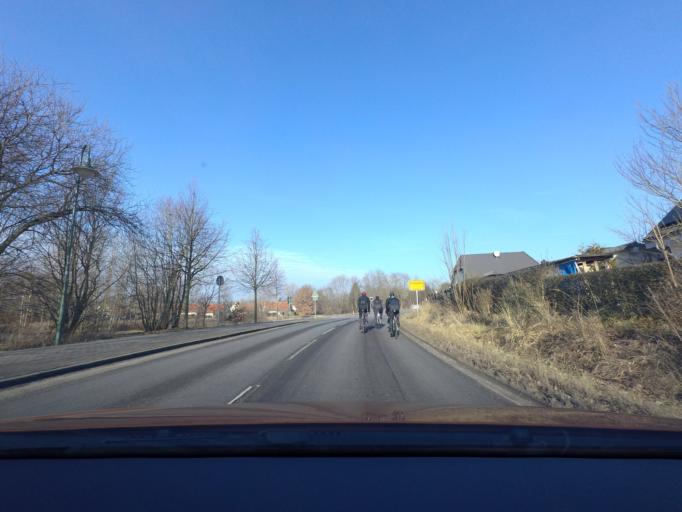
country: DE
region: Berlin
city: Blankenfelde
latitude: 52.6581
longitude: 13.3765
